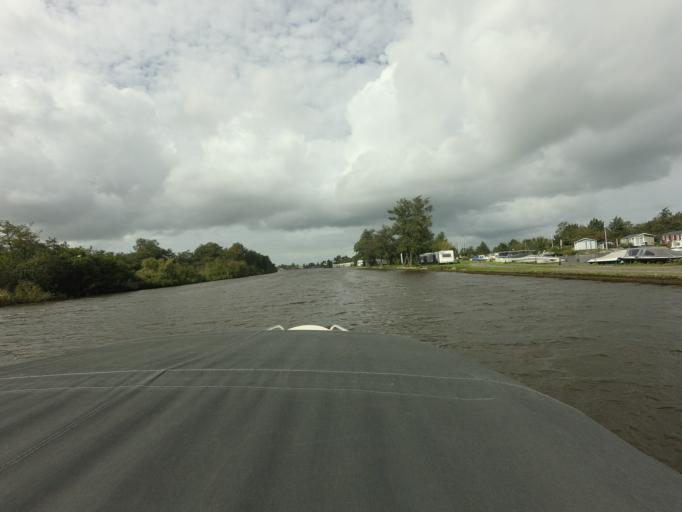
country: NL
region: Friesland
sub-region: Gemeente Boarnsterhim
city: Warten
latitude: 53.1254
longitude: 5.9387
